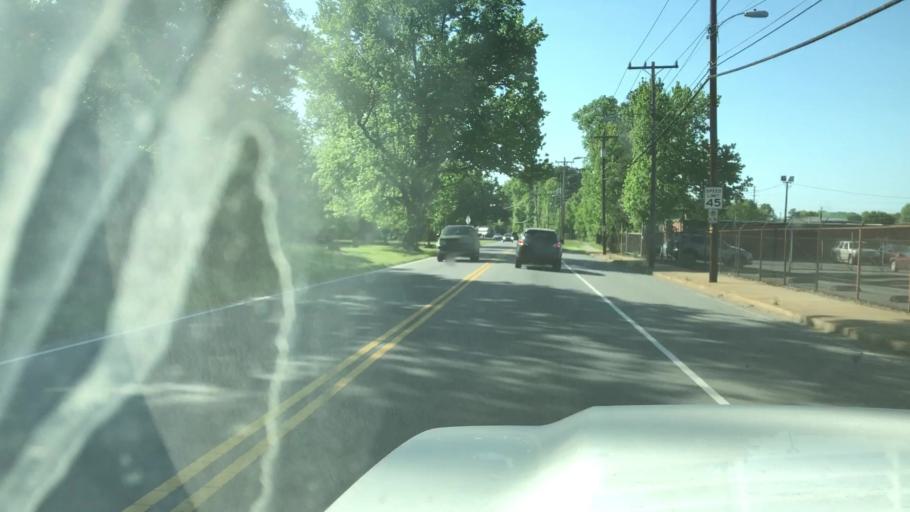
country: US
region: North Carolina
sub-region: Mecklenburg County
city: Charlotte
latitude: 35.2783
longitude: -80.8986
